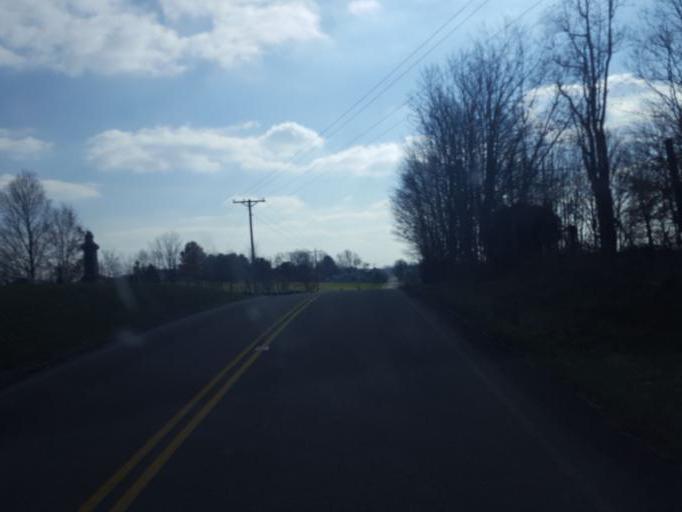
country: US
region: Ohio
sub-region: Knox County
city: Oak Hill
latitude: 40.4237
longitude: -82.1379
